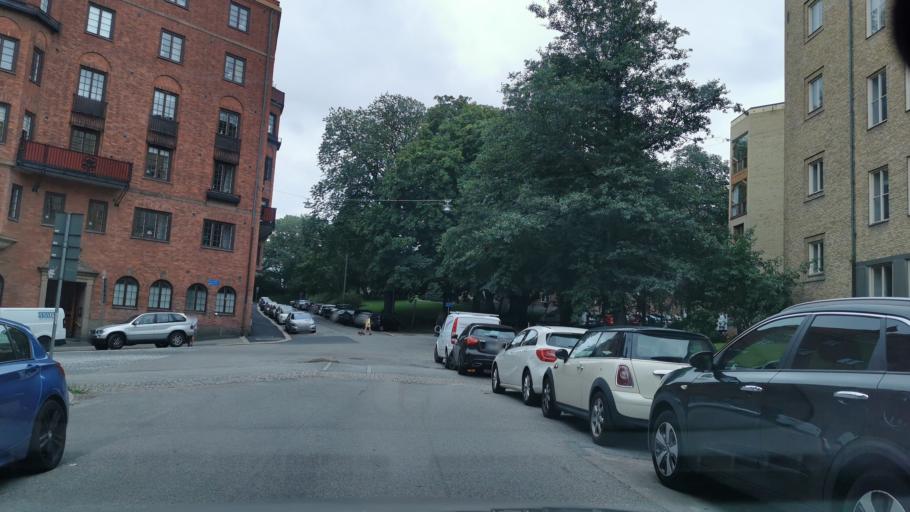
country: SE
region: Vaestra Goetaland
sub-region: Goteborg
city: Goeteborg
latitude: 57.6971
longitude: 11.9829
